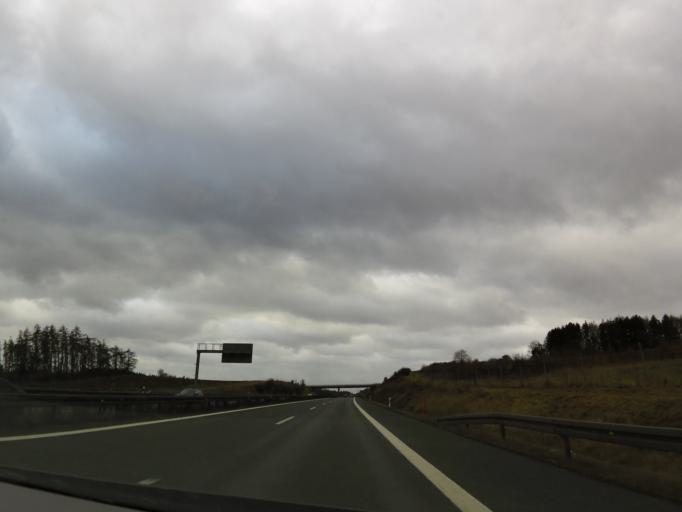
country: DE
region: Bavaria
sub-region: Upper Franconia
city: Trogen
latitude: 50.3647
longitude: 11.9733
